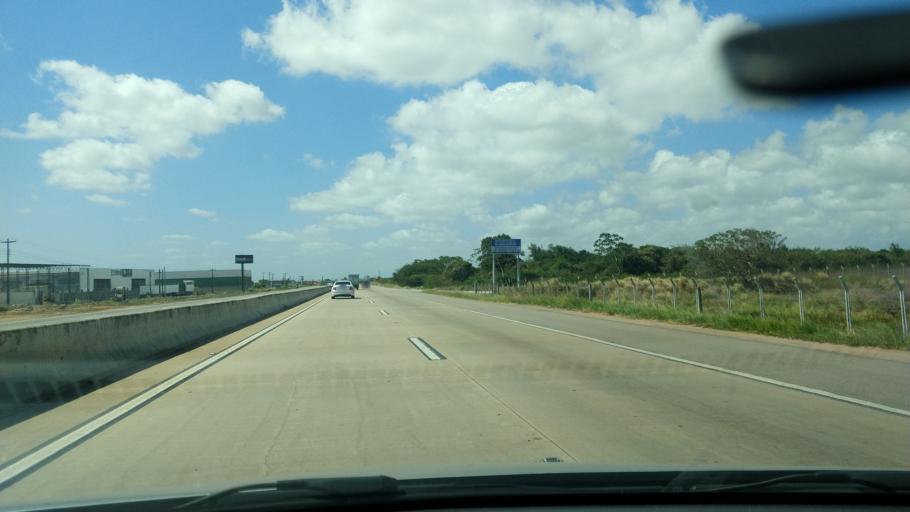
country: BR
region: Rio Grande do Norte
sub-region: Parnamirim
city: Parnamirim
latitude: -5.9927
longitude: -35.2630
